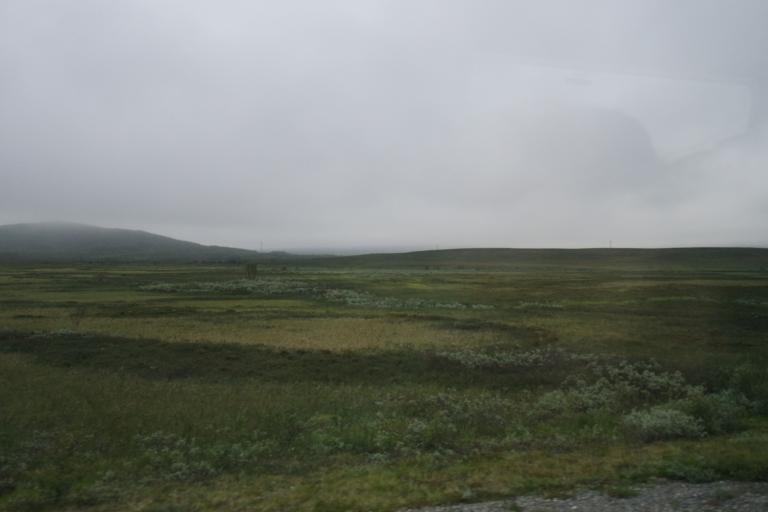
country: NO
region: Finnmark Fylke
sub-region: Kvalsund
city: Kvalsund
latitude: 70.2631
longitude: 24.0973
